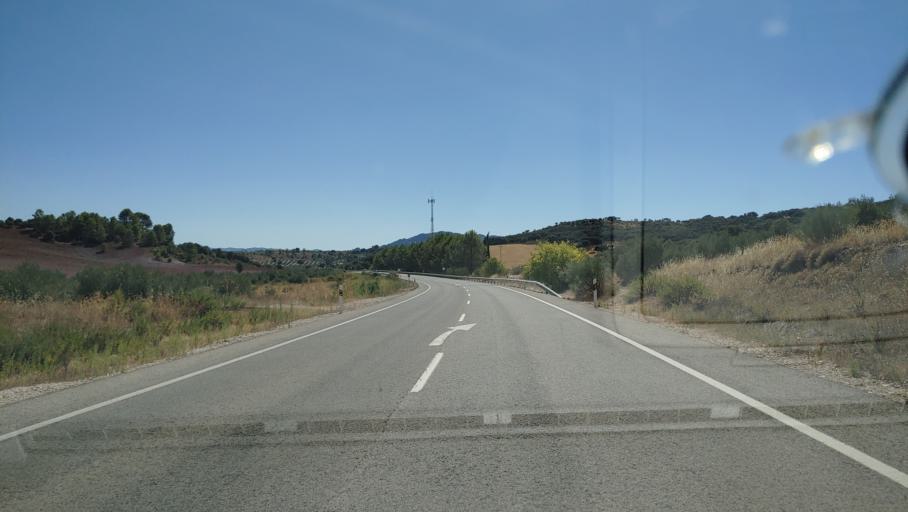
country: ES
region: Andalusia
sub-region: Provincia de Jaen
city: Genave
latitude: 38.4593
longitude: -2.7663
